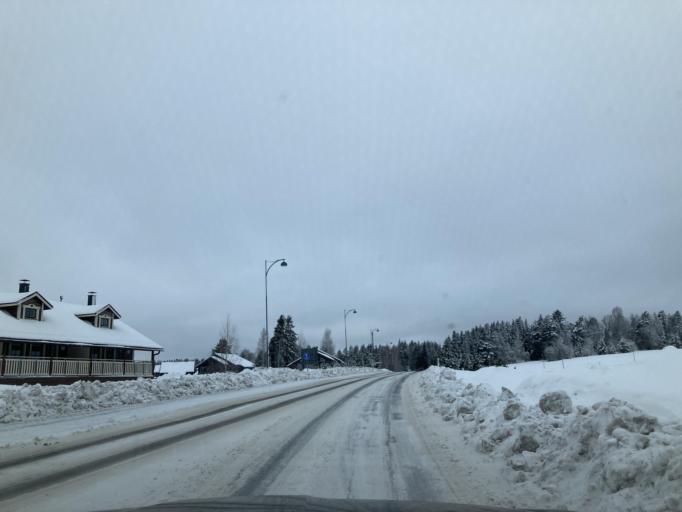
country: FI
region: Central Finland
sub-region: Jaemsae
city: Jaemsae
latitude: 61.8813
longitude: 25.2992
